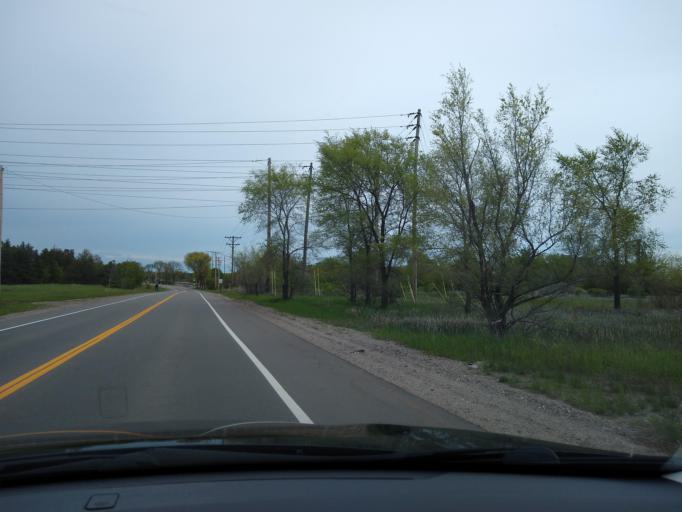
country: US
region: Michigan
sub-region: Delta County
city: Escanaba
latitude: 45.7682
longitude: -87.0691
